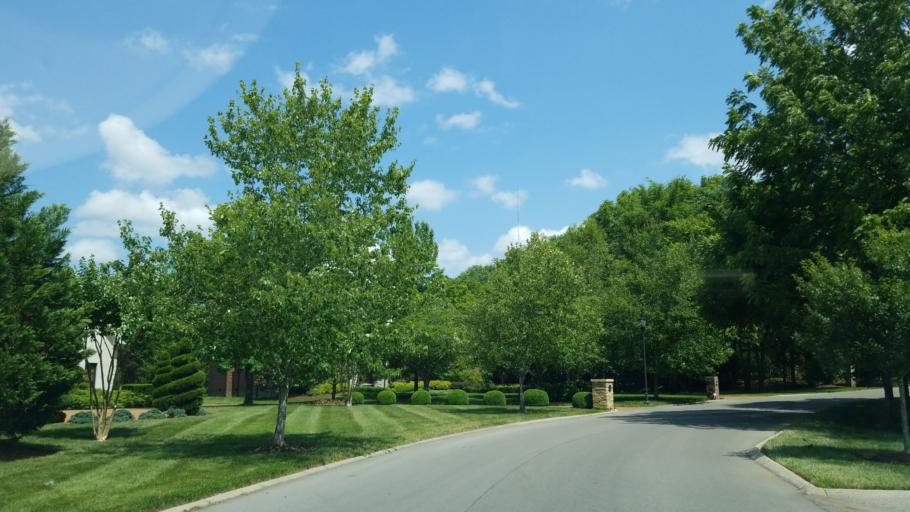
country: US
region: Tennessee
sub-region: Davidson County
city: Forest Hills
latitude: 36.0415
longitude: -86.8645
